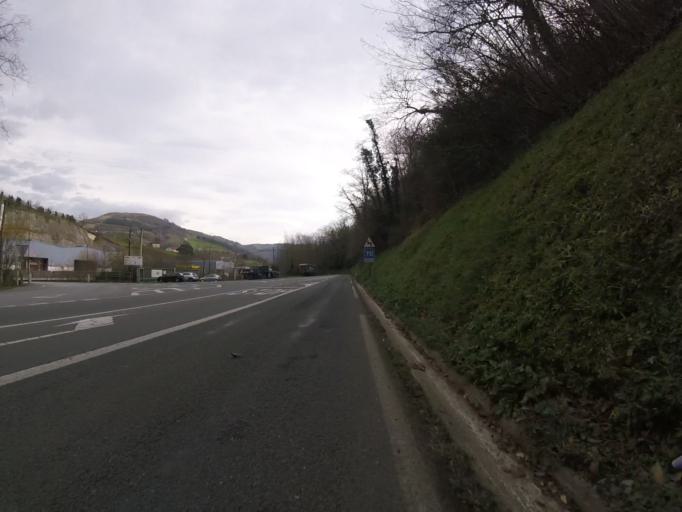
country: ES
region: Basque Country
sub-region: Provincia de Guipuzcoa
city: Aizarnazabal
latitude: 43.2536
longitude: -2.2439
